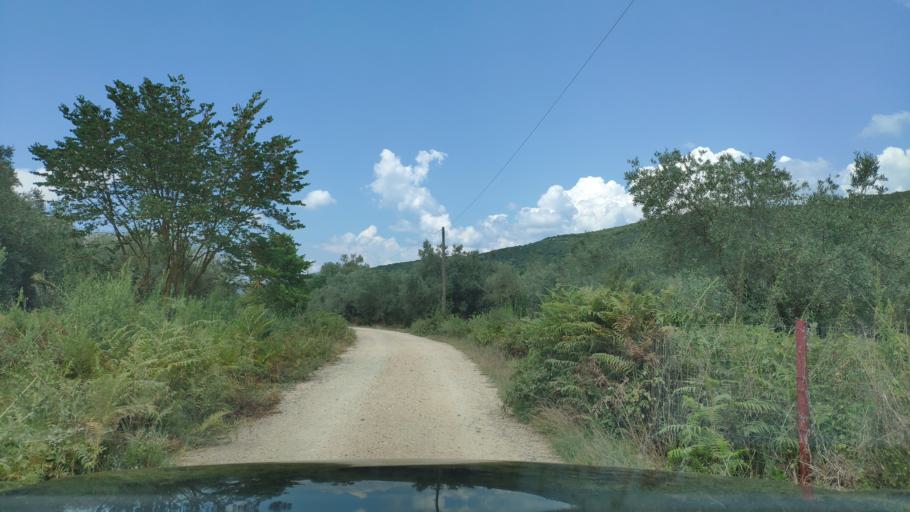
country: GR
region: West Greece
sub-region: Nomos Aitolias kai Akarnanias
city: Menidi
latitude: 39.0600
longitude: 21.0944
